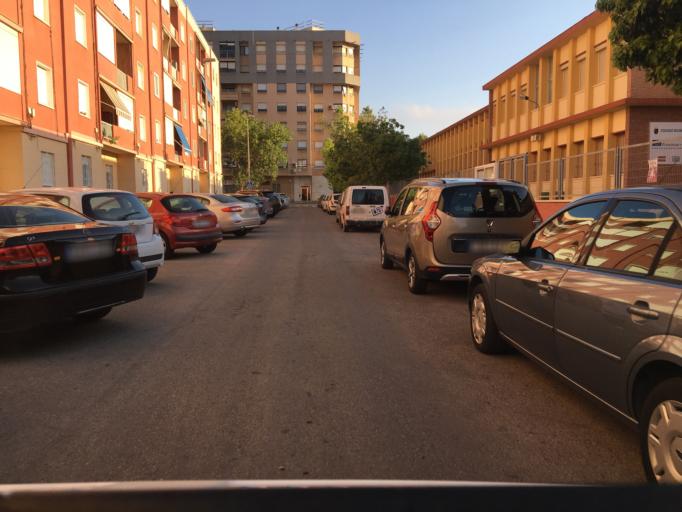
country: ES
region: Murcia
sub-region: Murcia
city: Cartagena
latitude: 37.6179
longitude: -0.9938
